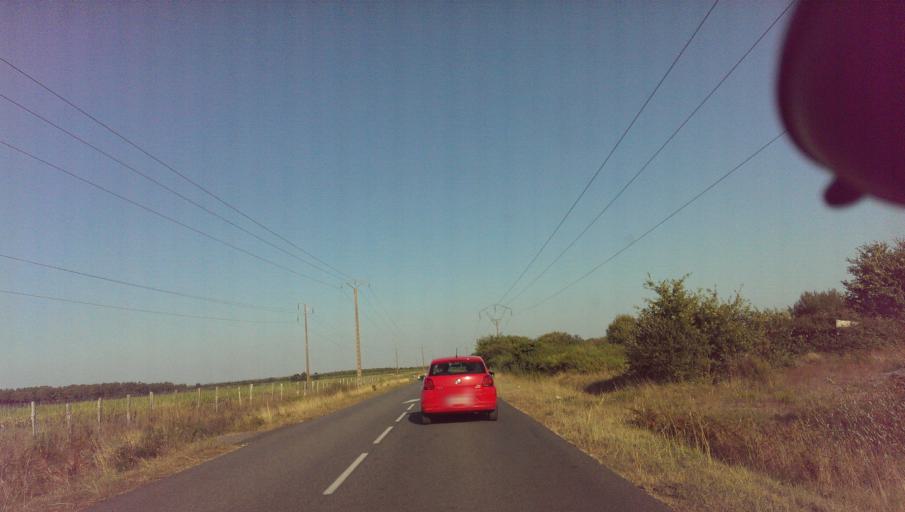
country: FR
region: Aquitaine
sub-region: Departement des Landes
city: Mimizan
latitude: 44.1872
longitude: -1.2051
